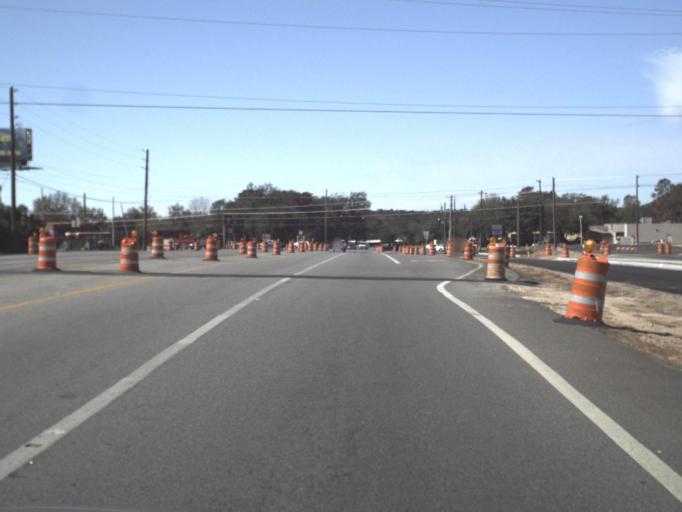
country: US
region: Florida
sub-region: Leon County
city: Tallahassee
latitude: 30.4362
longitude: -84.3511
